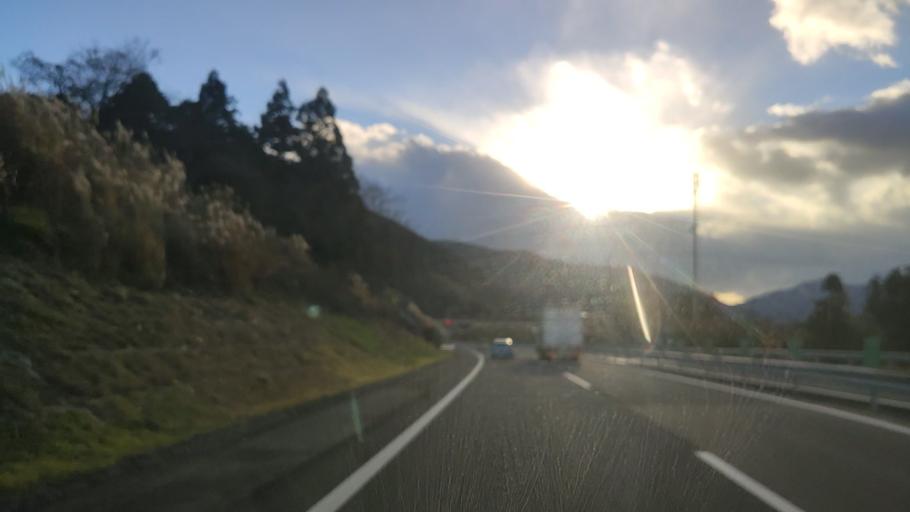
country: JP
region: Ehime
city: Saijo
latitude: 33.8694
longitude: 133.0602
